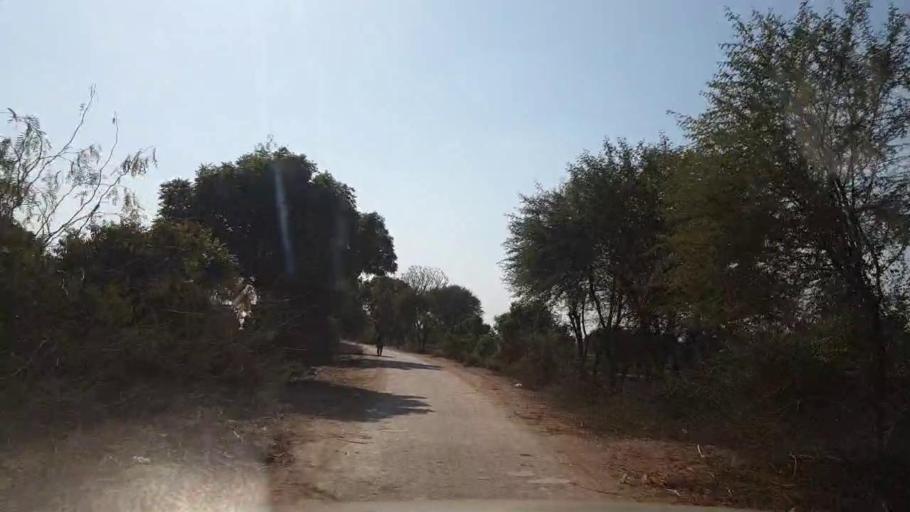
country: PK
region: Sindh
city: Tando Allahyar
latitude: 25.4759
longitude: 68.6947
